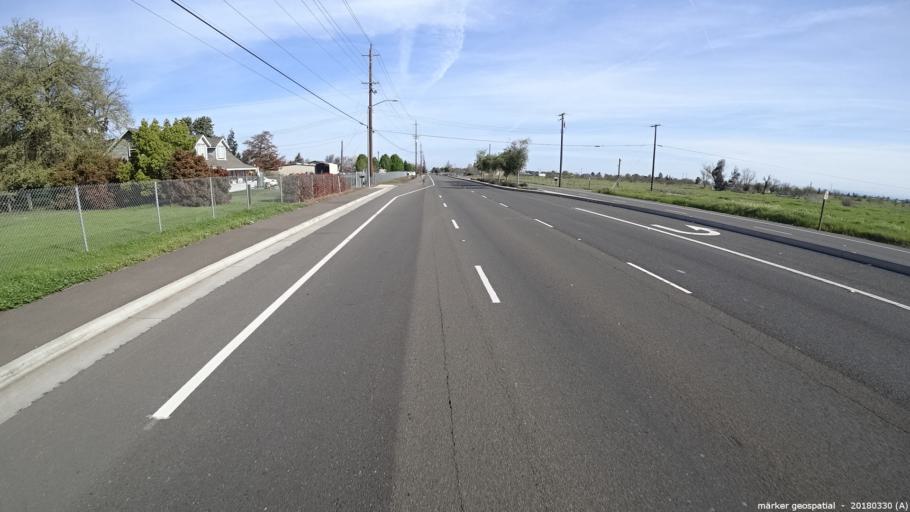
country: US
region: California
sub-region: Sacramento County
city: Vineyard
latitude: 38.4895
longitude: -121.3350
